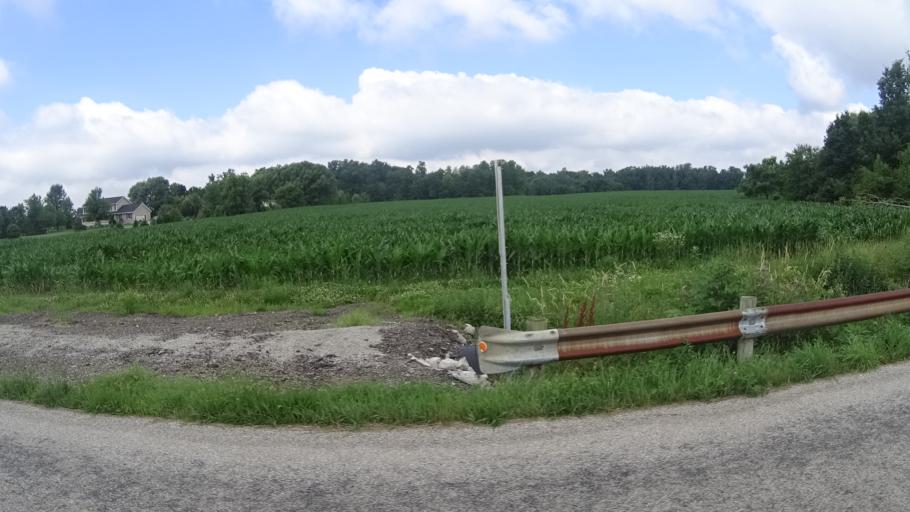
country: US
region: Ohio
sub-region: Huron County
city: Wakeman
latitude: 41.3166
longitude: -82.4509
